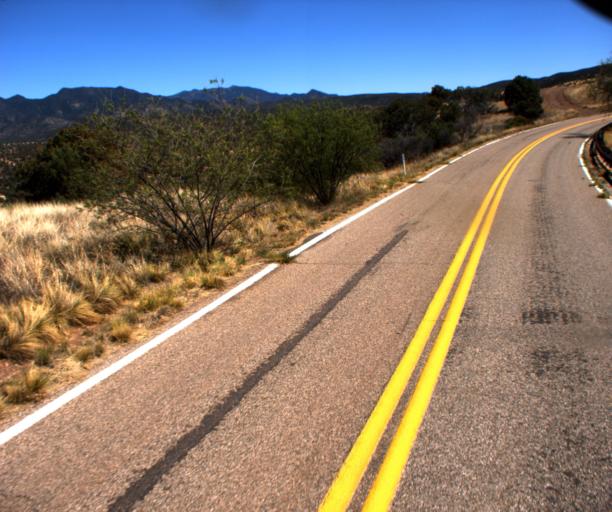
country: US
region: Arizona
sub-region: Cochise County
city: Sierra Vista
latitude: 31.5013
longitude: -110.4944
